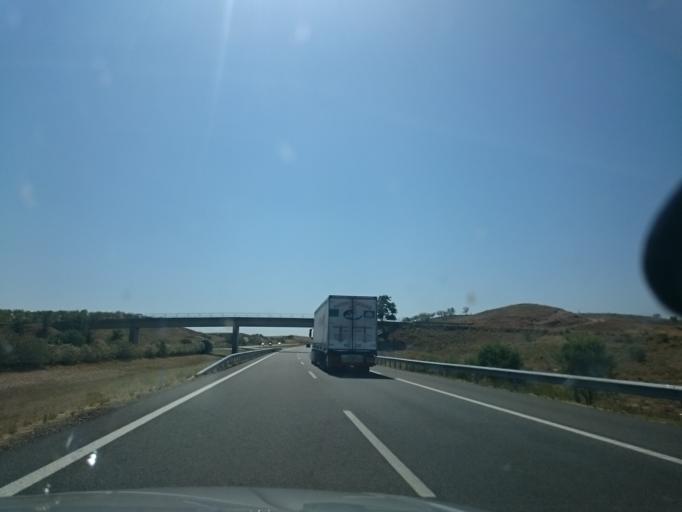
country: ES
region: Navarre
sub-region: Provincia de Navarra
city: Ribaforada
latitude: 41.9794
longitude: -1.5564
